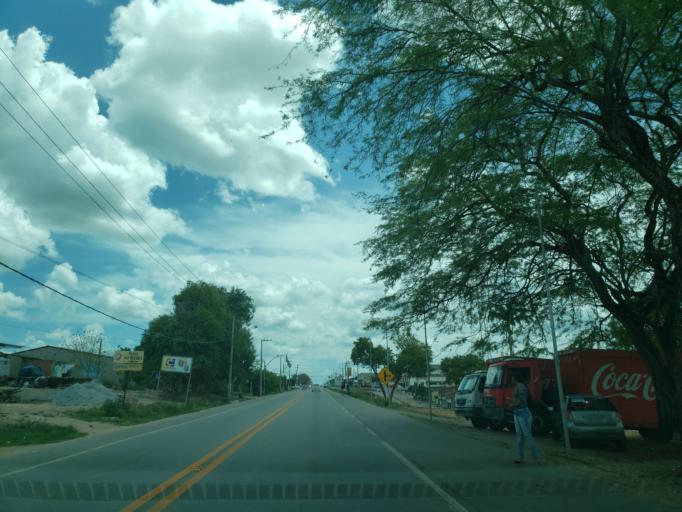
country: BR
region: Alagoas
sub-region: Uniao Dos Palmares
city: Uniao dos Palmares
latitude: -9.1648
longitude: -36.0197
